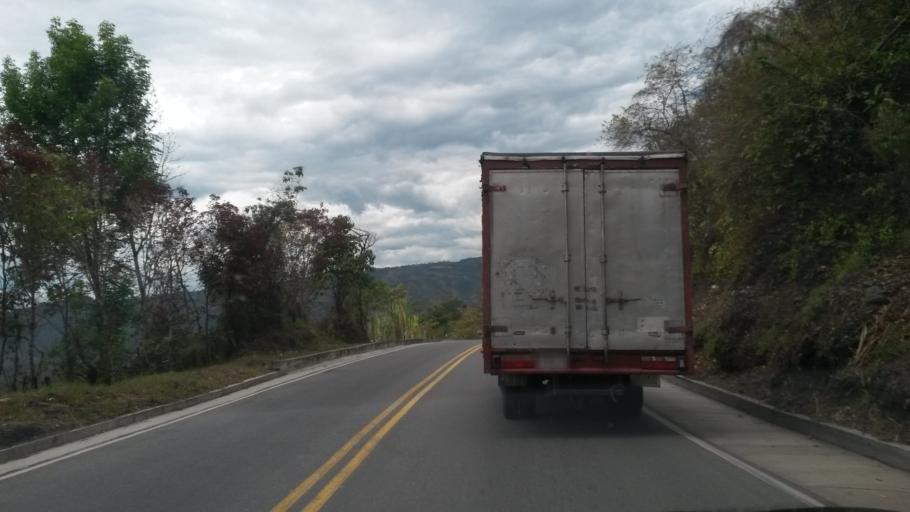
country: CO
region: Cauca
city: Rosas
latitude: 2.2660
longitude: -76.7360
